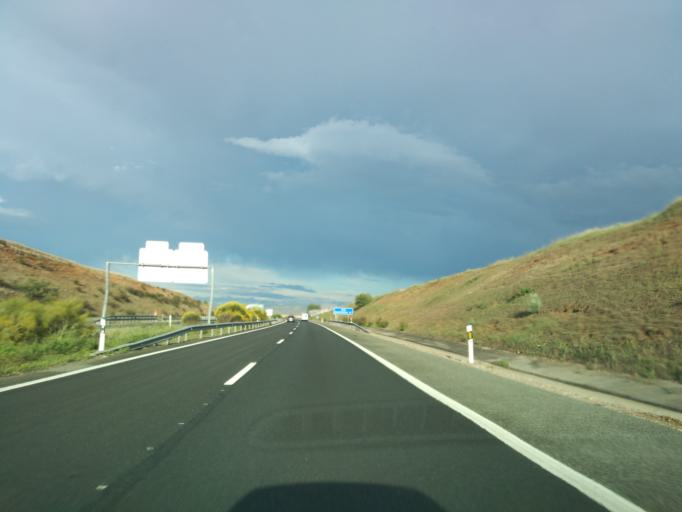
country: ES
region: Madrid
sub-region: Provincia de Madrid
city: Ajalvir
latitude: 40.5067
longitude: -3.4784
